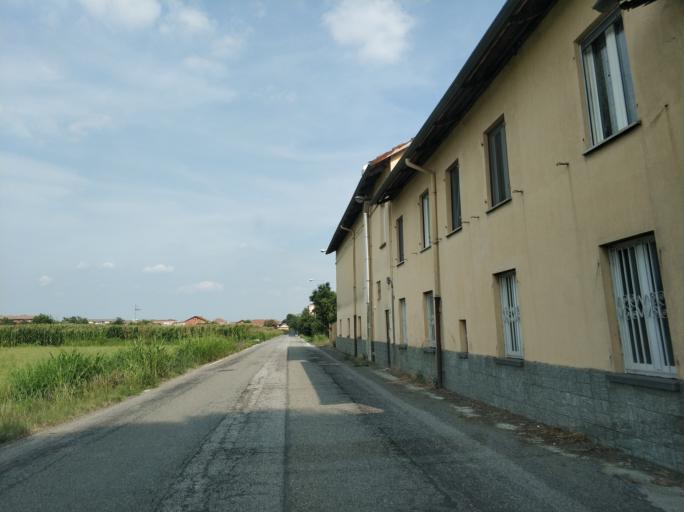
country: IT
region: Piedmont
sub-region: Provincia di Torino
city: Borgaro Torinese
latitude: 45.1507
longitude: 7.6913
